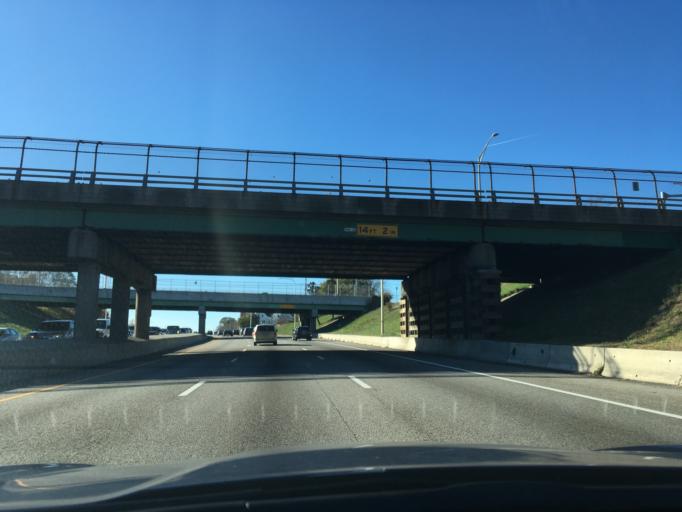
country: US
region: Rhode Island
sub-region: Providence County
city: Pawtucket
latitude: 41.8732
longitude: -71.3891
